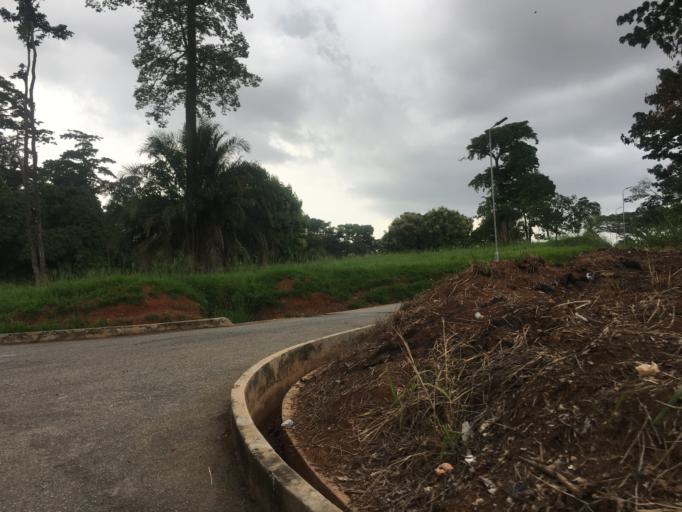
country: GH
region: Ashanti
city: Kumasi
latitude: 6.6726
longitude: -1.5754
